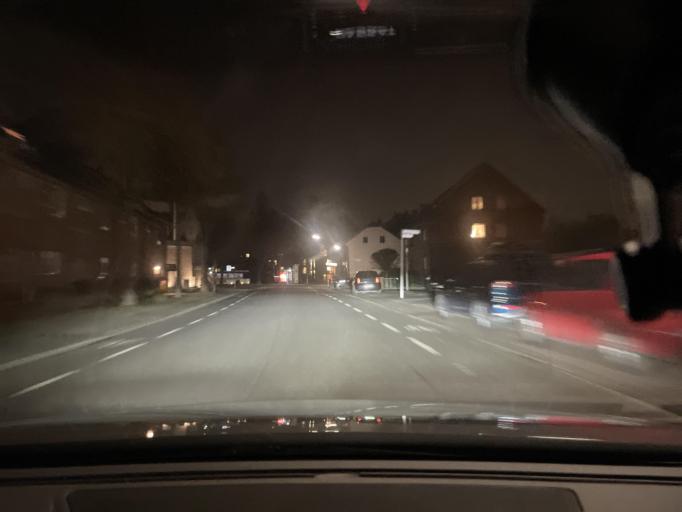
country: DE
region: North Rhine-Westphalia
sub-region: Regierungsbezirk Dusseldorf
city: Monchengladbach
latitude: 51.2208
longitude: 6.4706
